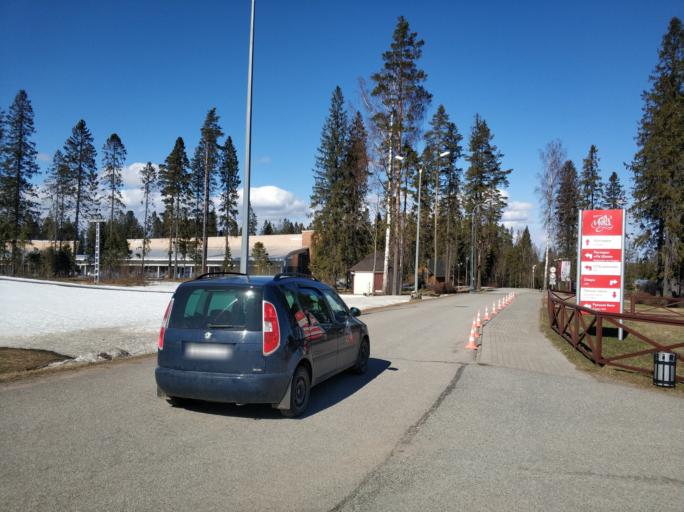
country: RU
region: Leningrad
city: Sosnovo
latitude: 60.5156
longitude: 30.2106
